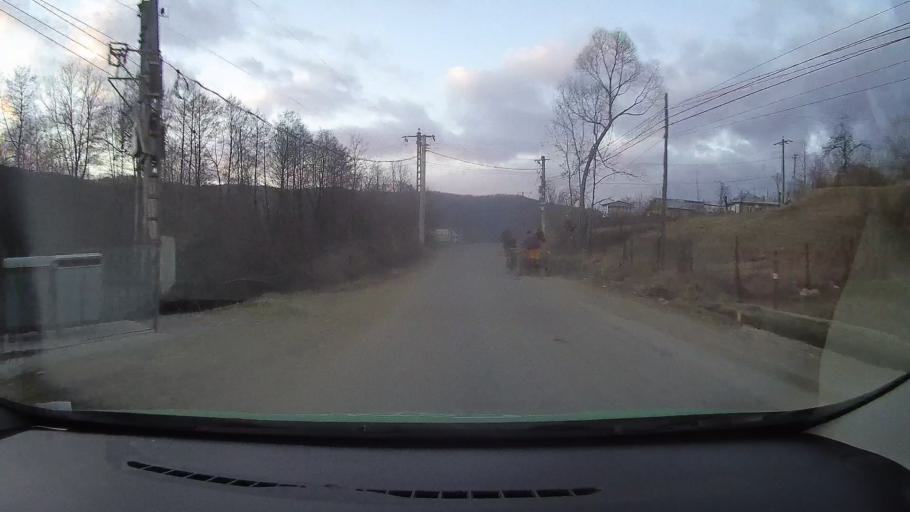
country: RO
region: Dambovita
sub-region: Comuna Valea Lunga
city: Valea Lunga-Cricov
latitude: 45.0728
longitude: 25.5780
